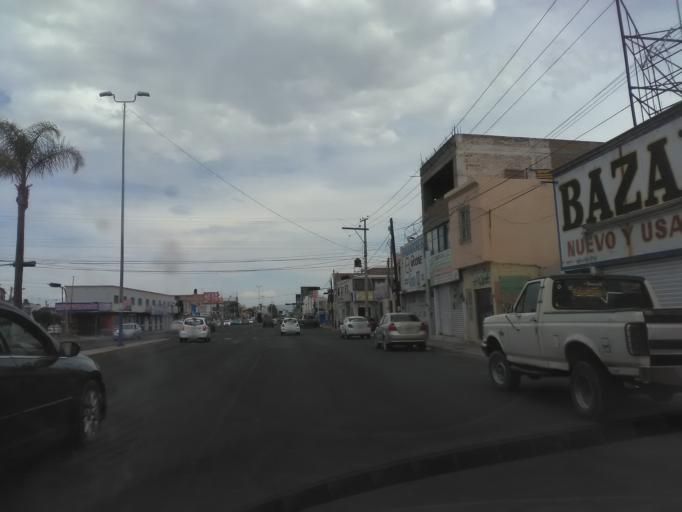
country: MX
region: Durango
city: Victoria de Durango
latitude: 24.0189
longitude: -104.6579
